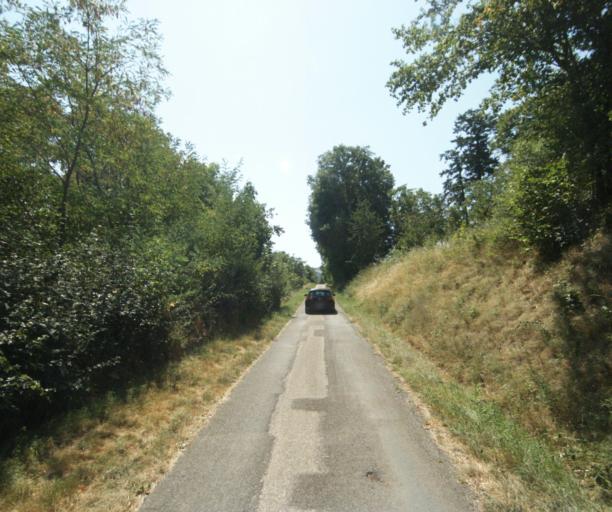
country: FR
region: Rhone-Alpes
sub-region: Departement du Rhone
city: Saint-Pierre-la-Palud
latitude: 45.7945
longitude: 4.6066
